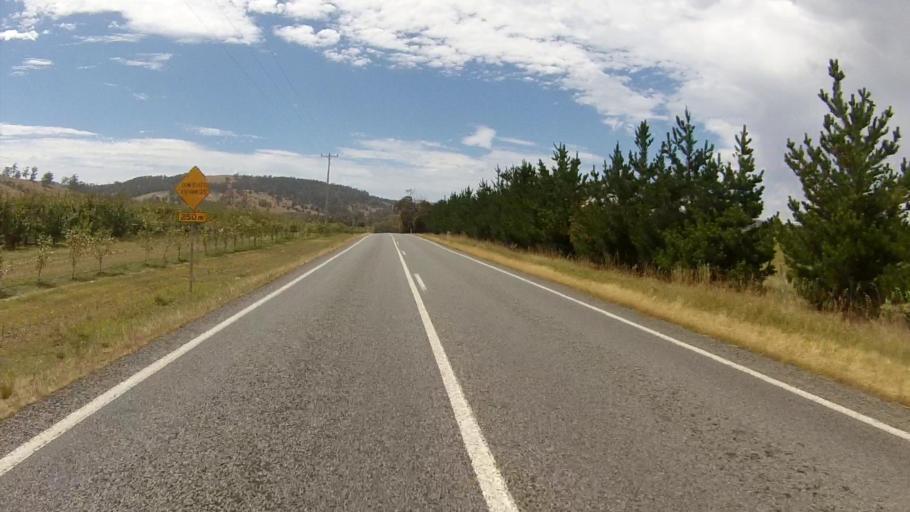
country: AU
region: Tasmania
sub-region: Sorell
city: Sorell
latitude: -42.6894
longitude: 147.4578
